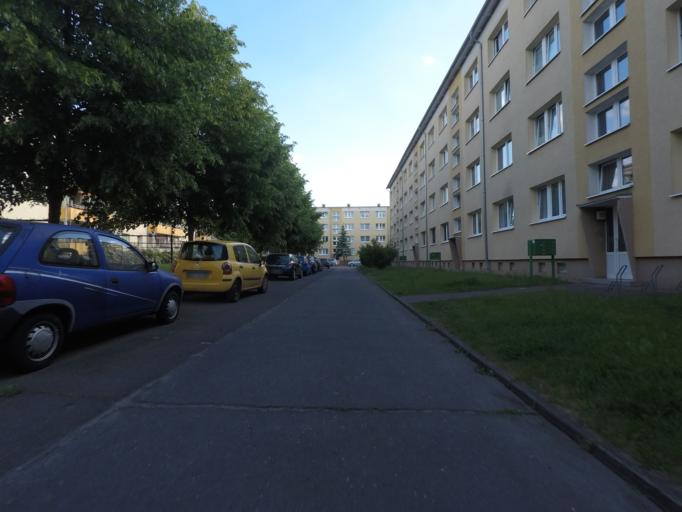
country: DE
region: Brandenburg
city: Eberswalde
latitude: 52.8396
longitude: 13.8098
